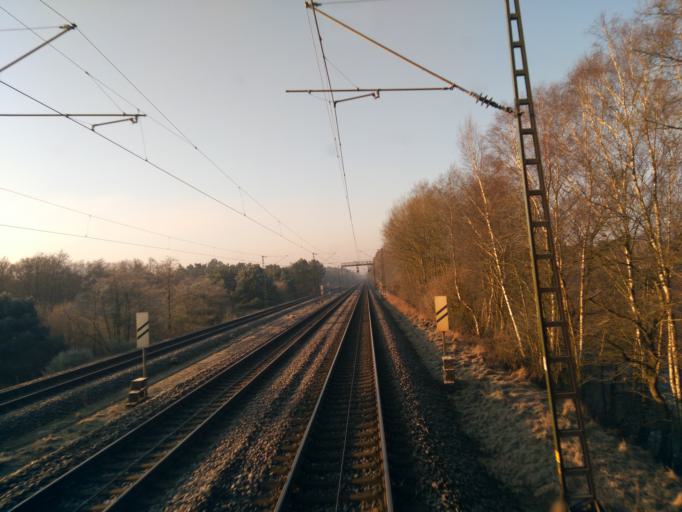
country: DE
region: Lower Saxony
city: Kakenstorf
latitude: 53.2917
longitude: 9.7744
